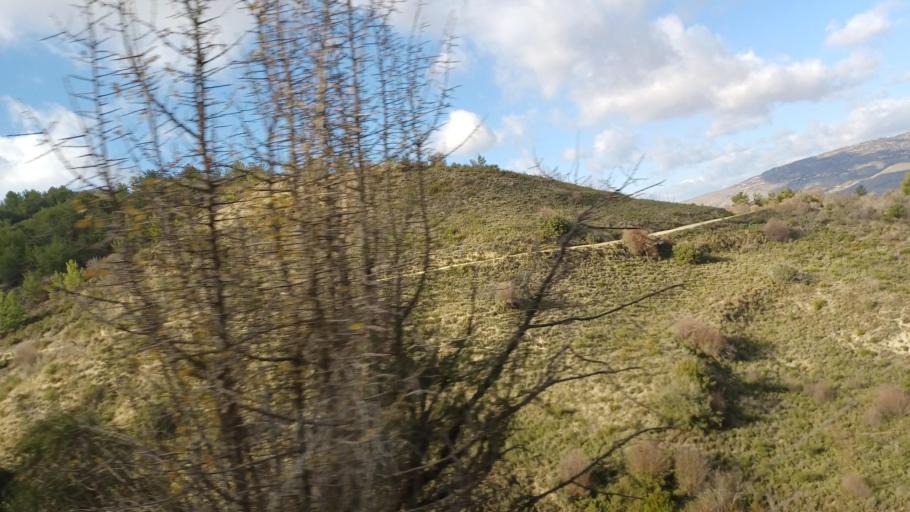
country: CY
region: Limassol
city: Pachna
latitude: 34.8543
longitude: 32.6896
